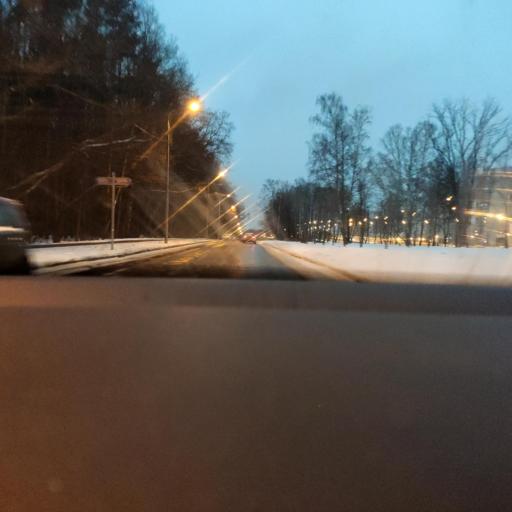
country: RU
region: Moskovskaya
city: Bol'shaya Setun'
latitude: 55.7477
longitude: 37.4145
